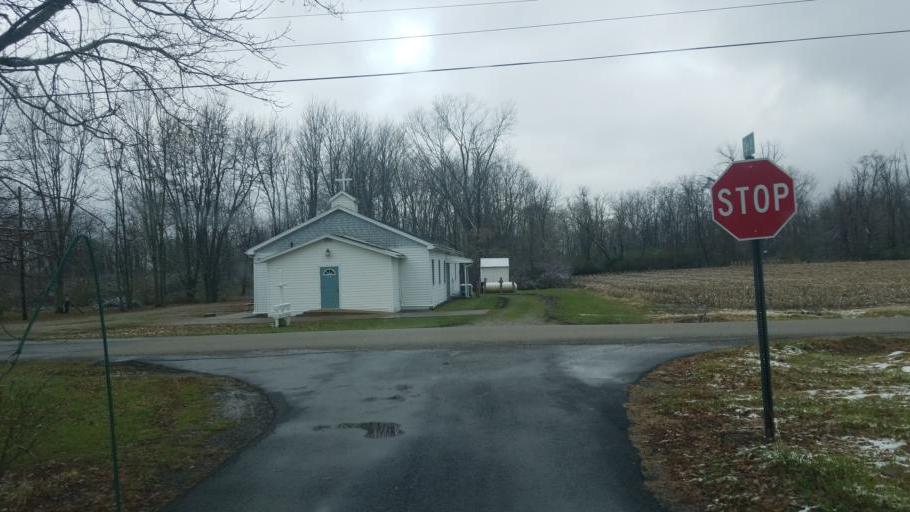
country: US
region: Ohio
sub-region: Richland County
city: Shelby
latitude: 40.9012
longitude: -82.6547
